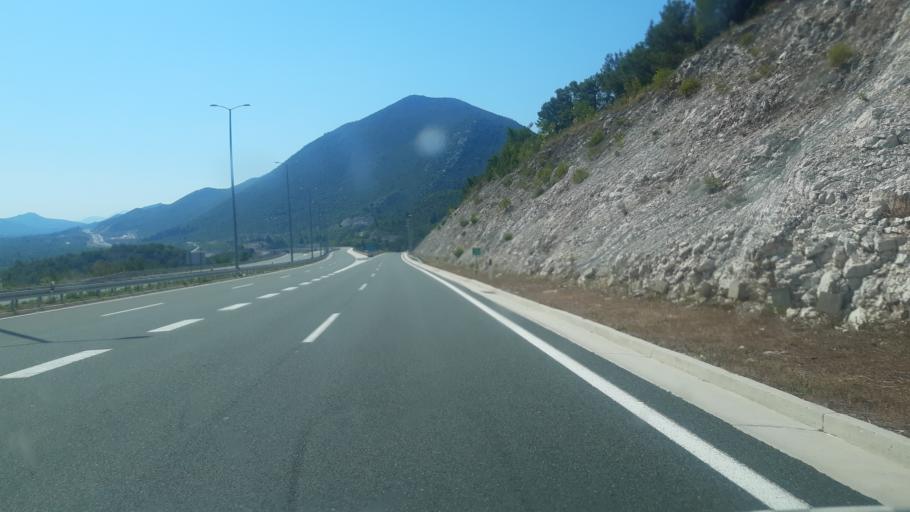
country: BA
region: Federation of Bosnia and Herzegovina
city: Ljubuski
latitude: 43.1531
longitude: 17.4808
